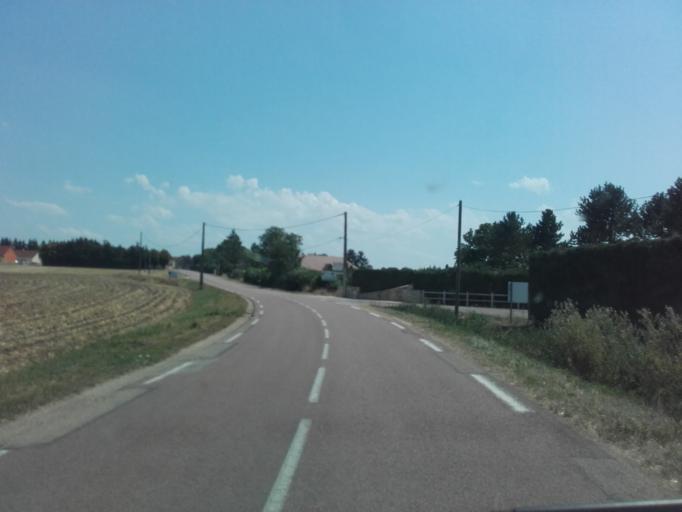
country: FR
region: Bourgogne
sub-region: Departement de l'Yonne
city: Joux-la-Ville
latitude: 47.6769
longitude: 3.8738
